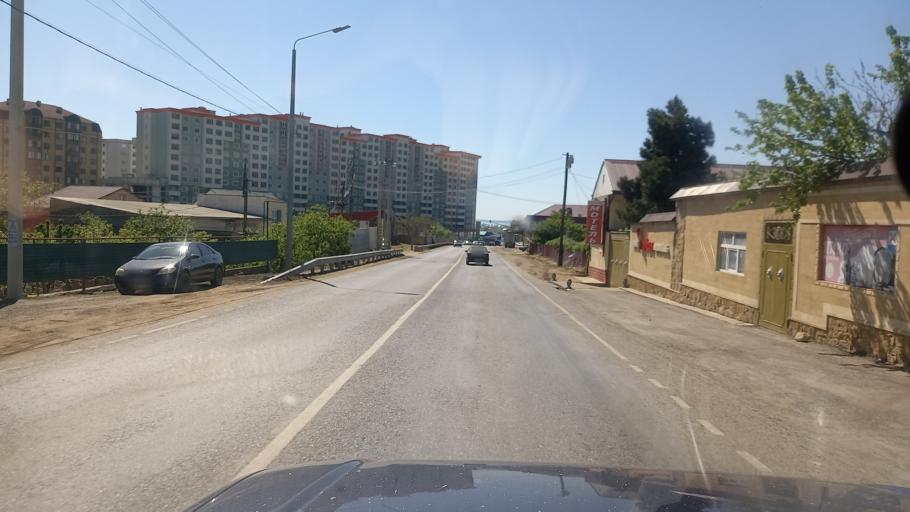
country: RU
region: Dagestan
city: Derbent
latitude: 42.0374
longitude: 48.2922
